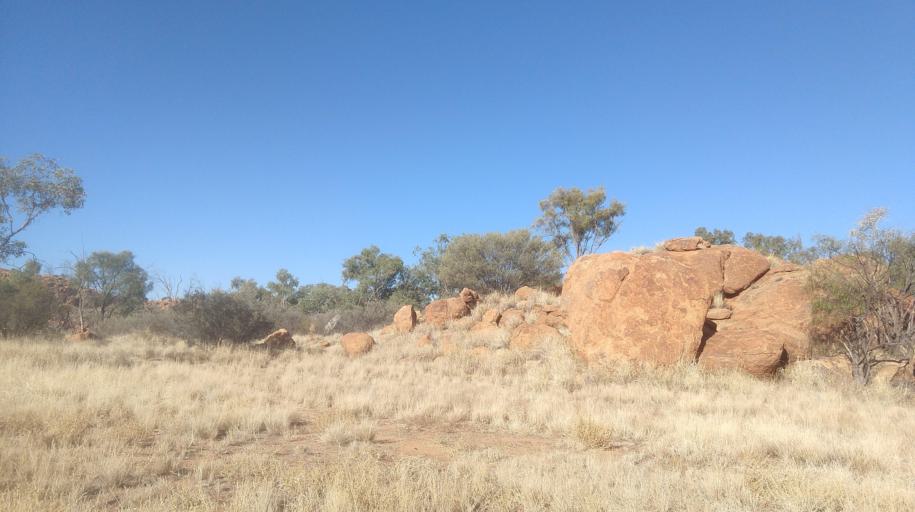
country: AU
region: Northern Territory
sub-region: Alice Springs
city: Alice Springs
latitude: -23.6707
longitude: 133.8851
